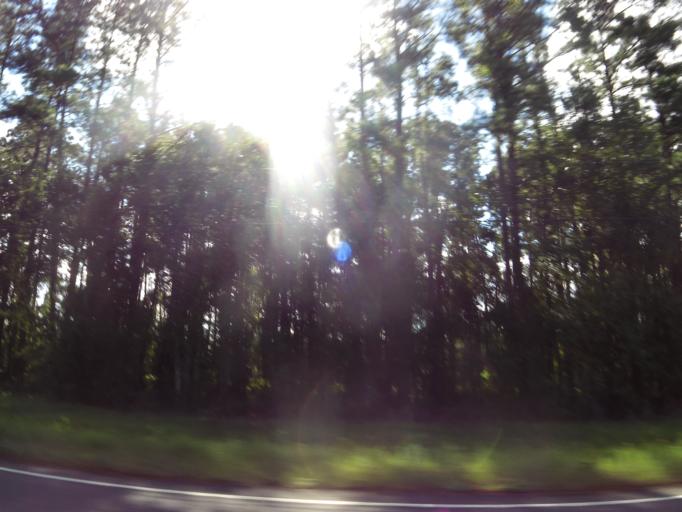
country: US
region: Georgia
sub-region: Camden County
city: Woodbine
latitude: 31.0249
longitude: -81.7309
